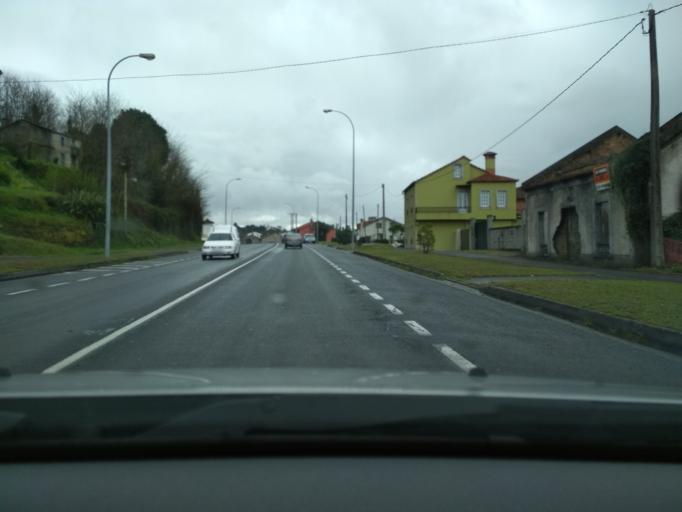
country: ES
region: Galicia
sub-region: Provincia da Coruna
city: Padron
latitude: 42.7638
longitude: -8.6518
